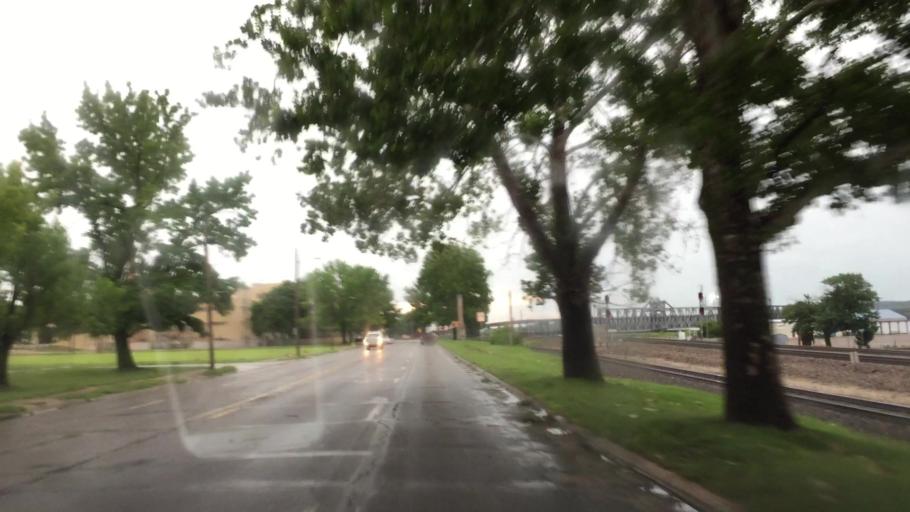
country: US
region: Iowa
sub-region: Lee County
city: Fort Madison
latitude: 40.6298
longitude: -91.3063
